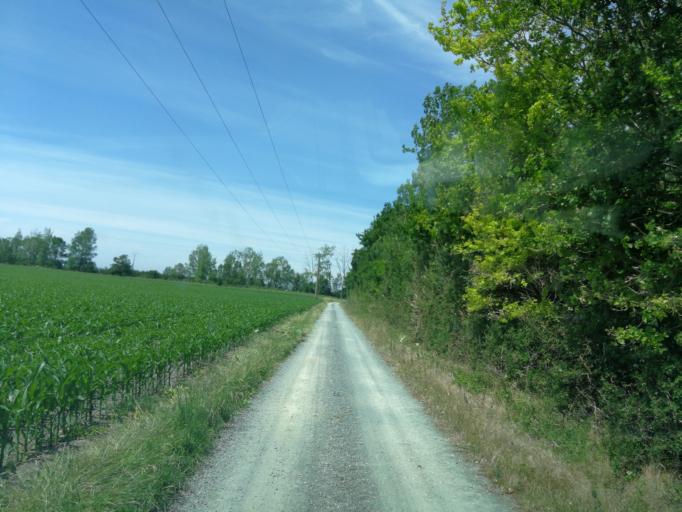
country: FR
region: Poitou-Charentes
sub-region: Departement de la Charente-Maritime
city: Marans
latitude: 46.3661
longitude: -0.9595
